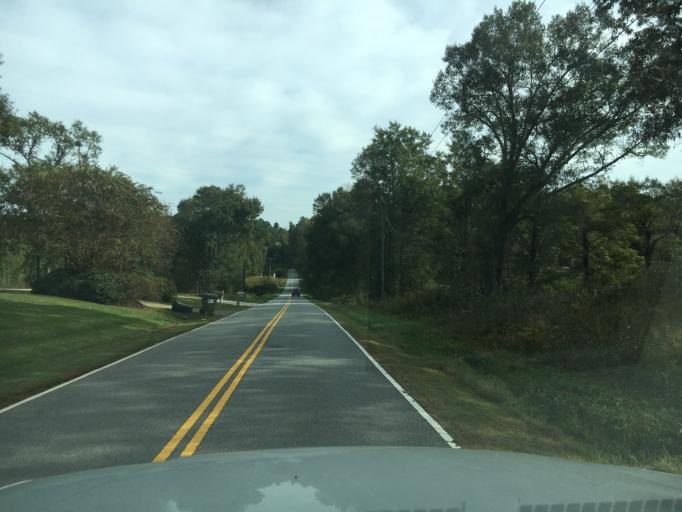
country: US
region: South Carolina
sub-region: Spartanburg County
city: Duncan
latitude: 34.9183
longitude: -82.1424
